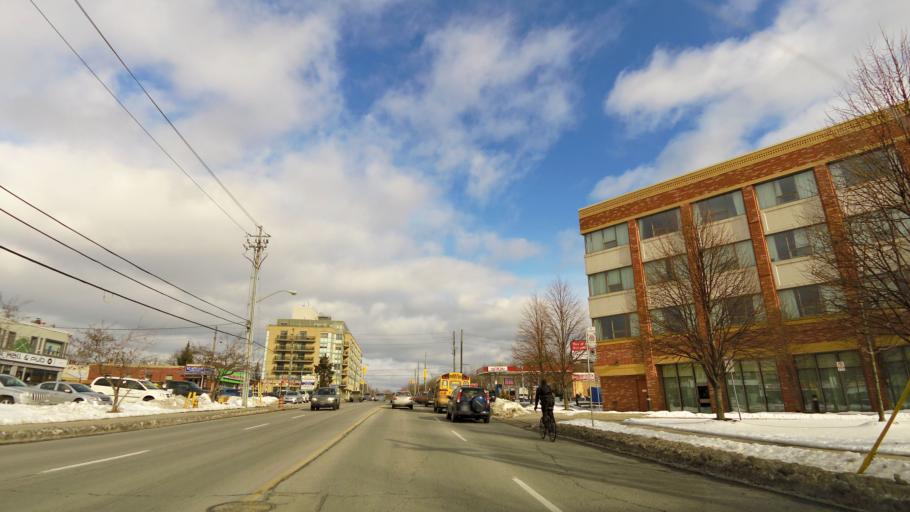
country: CA
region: Ontario
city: Scarborough
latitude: 43.6941
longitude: -79.2750
